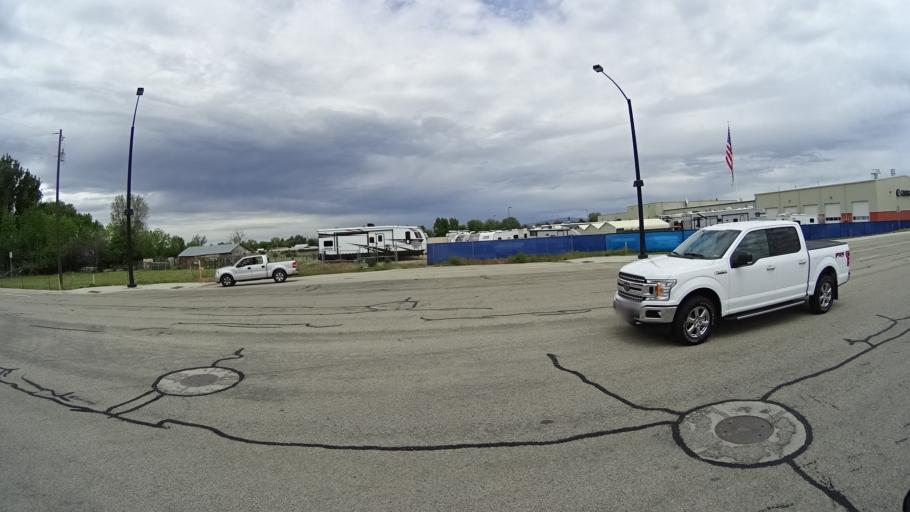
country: US
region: Idaho
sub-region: Ada County
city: Meridian
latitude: 43.5901
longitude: -116.4136
